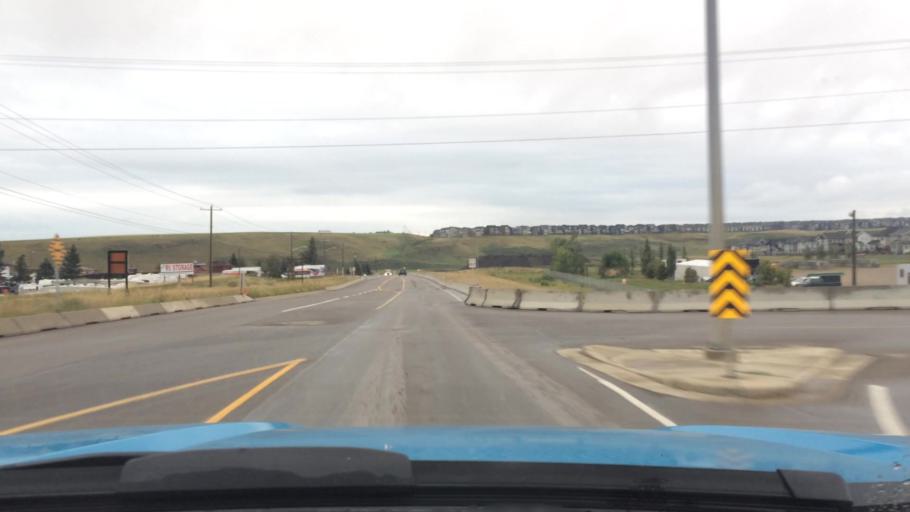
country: CA
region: Alberta
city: Calgary
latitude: 51.1830
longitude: -114.1416
